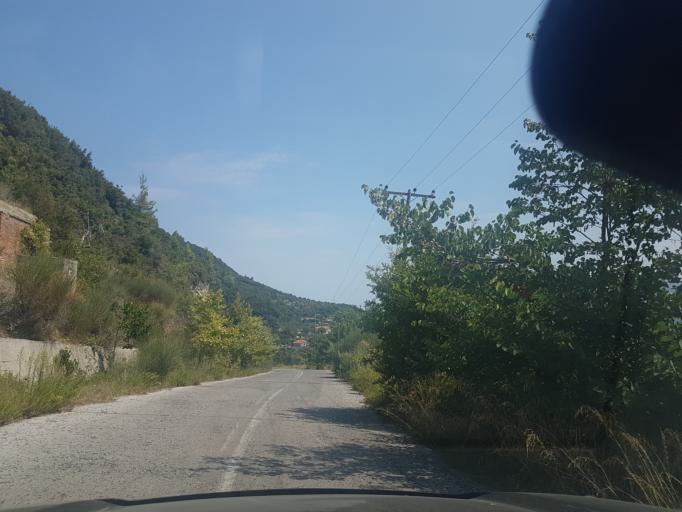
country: GR
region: Central Greece
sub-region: Nomos Evvoias
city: Kymi
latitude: 38.6482
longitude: 23.9016
